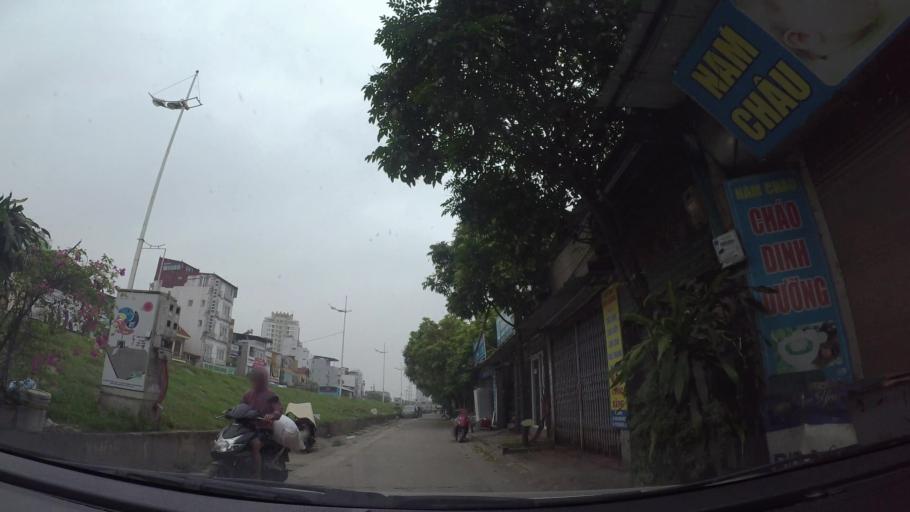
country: VN
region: Ha Noi
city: Tay Ho
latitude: 21.0792
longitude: 105.8202
